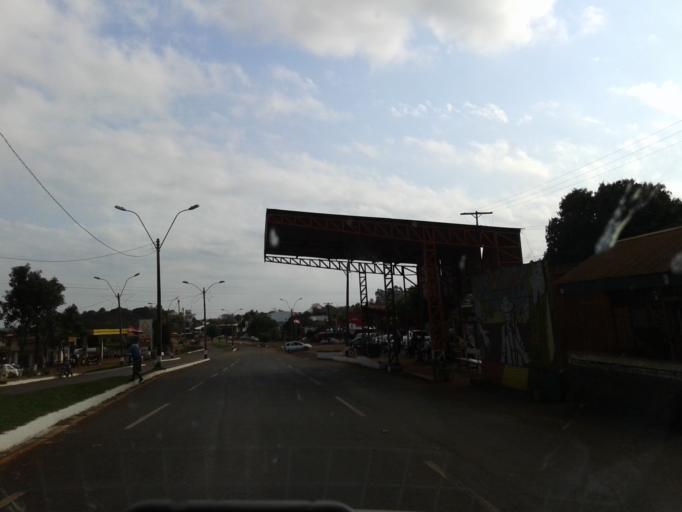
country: PY
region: Itapua
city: Edelira
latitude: -26.7223
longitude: -55.3425
